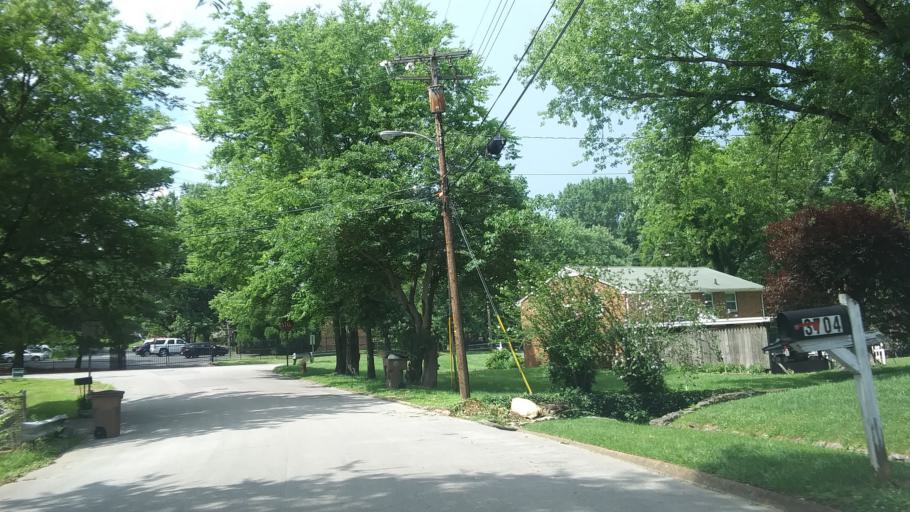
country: US
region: Tennessee
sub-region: Davidson County
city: Oak Hill
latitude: 36.0786
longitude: -86.7047
